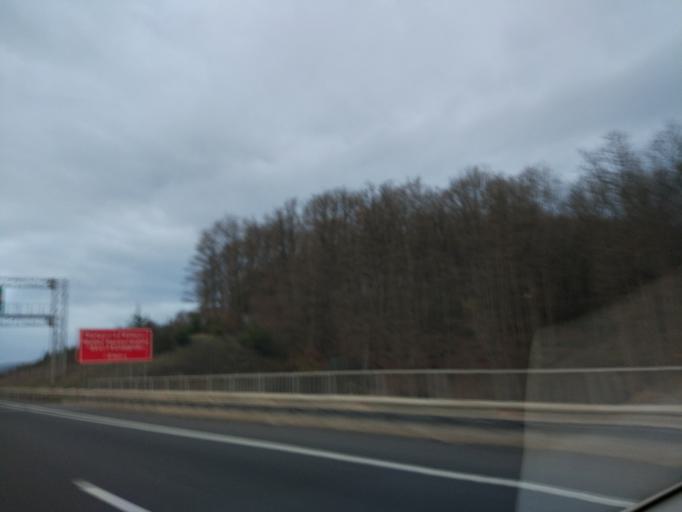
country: TR
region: Bolu
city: Bolu
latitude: 40.7208
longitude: 31.4869
